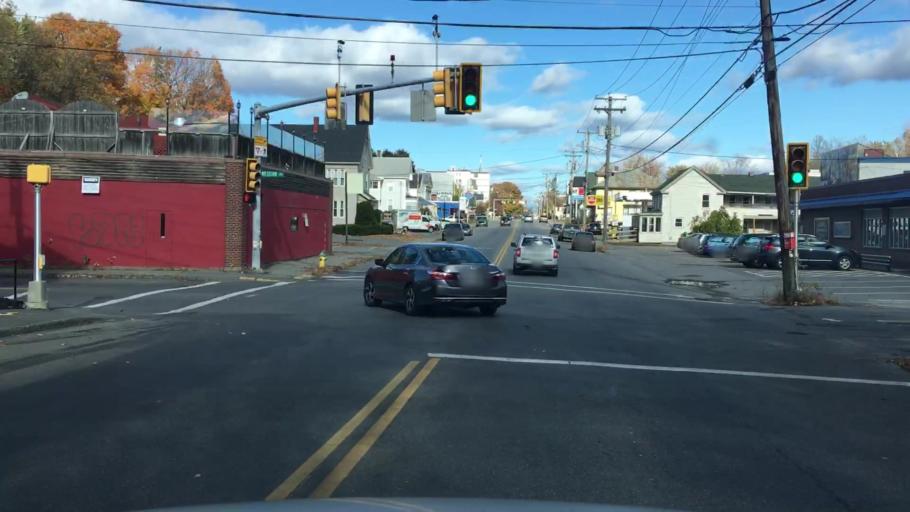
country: US
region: Maine
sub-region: Kennebec County
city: Waterville
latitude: 44.5472
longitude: -69.6353
